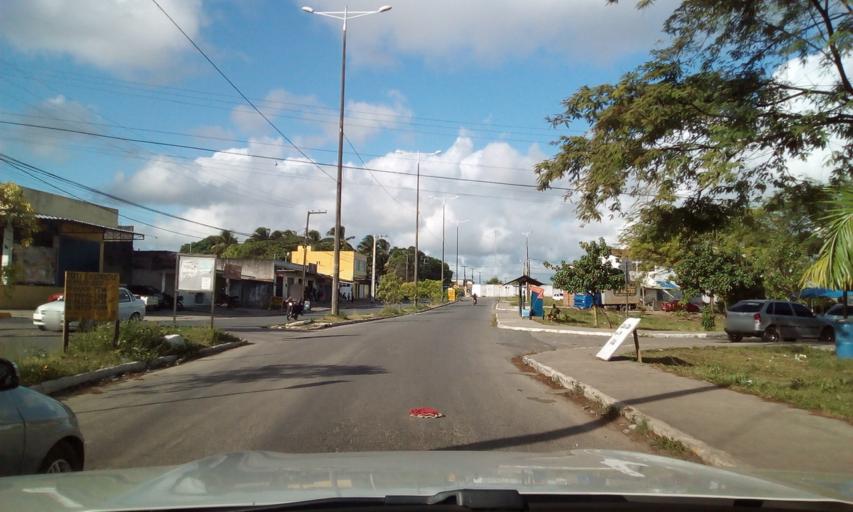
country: BR
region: Paraiba
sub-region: Bayeux
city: Bayeux
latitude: -7.1776
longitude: -34.9139
